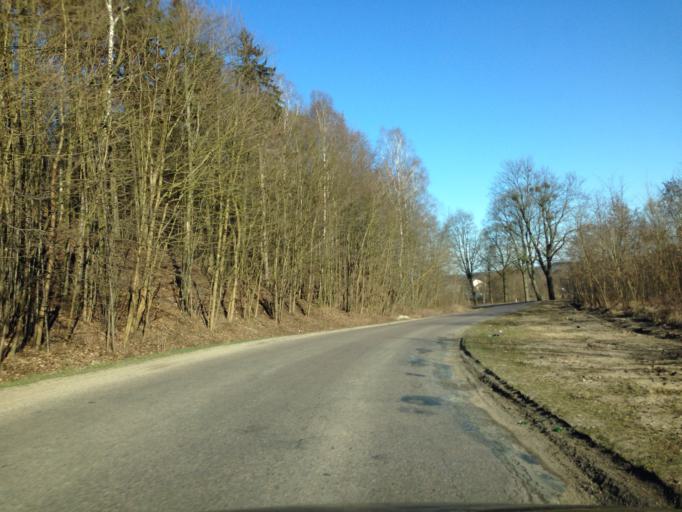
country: PL
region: Warmian-Masurian Voivodeship
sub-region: Powiat nowomiejski
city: Nowe Miasto Lubawskie
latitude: 53.4066
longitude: 19.6030
